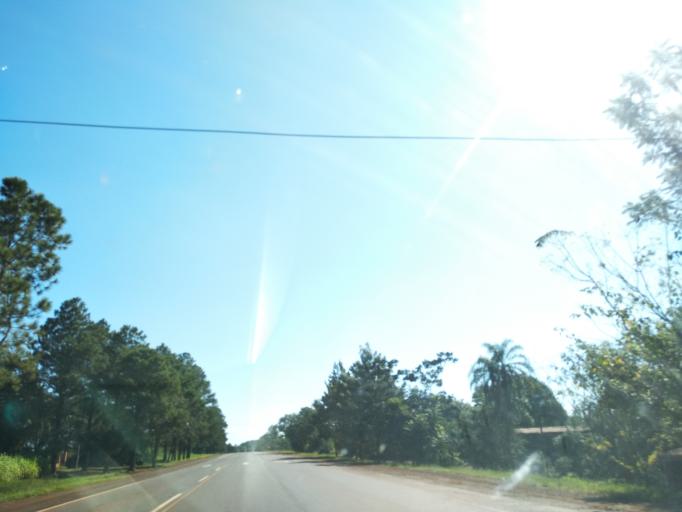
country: AR
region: Misiones
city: Garuhape
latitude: -26.8218
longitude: -54.9718
